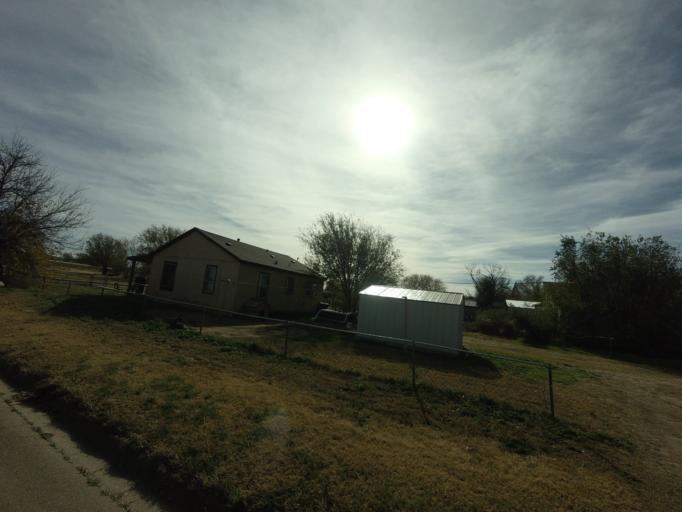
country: US
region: New Mexico
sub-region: Curry County
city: Clovis
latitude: 34.4057
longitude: -103.1931
